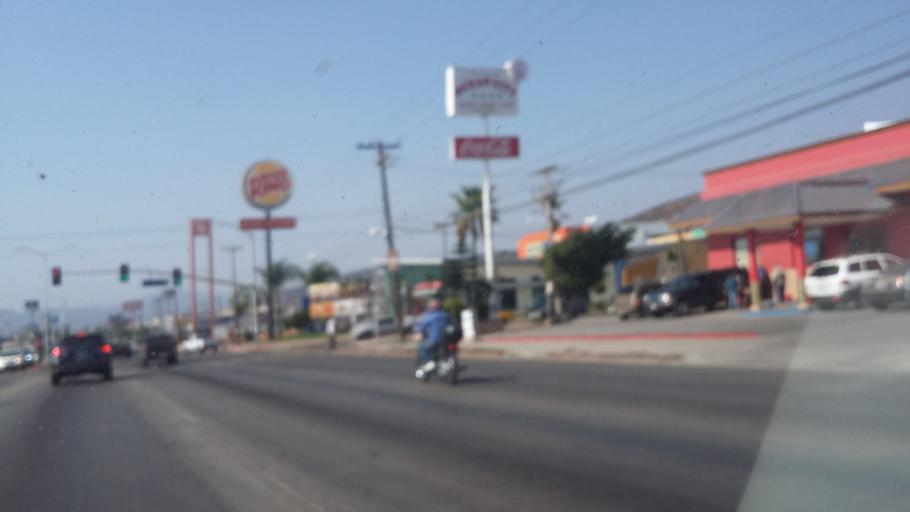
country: MX
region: Baja California
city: Ensenada
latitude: 31.8139
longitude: -116.5974
